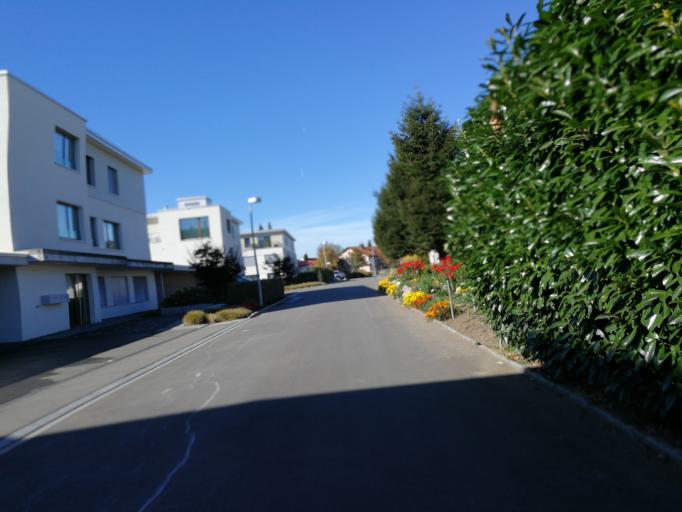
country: CH
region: Saint Gallen
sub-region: Wahlkreis See-Gaster
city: Jona
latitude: 47.2193
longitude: 8.8357
